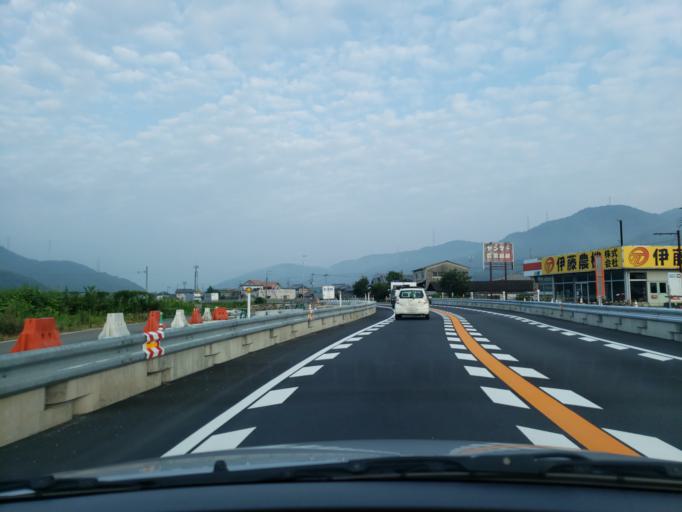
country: JP
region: Hyogo
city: Aioi
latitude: 34.8330
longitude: 134.4291
